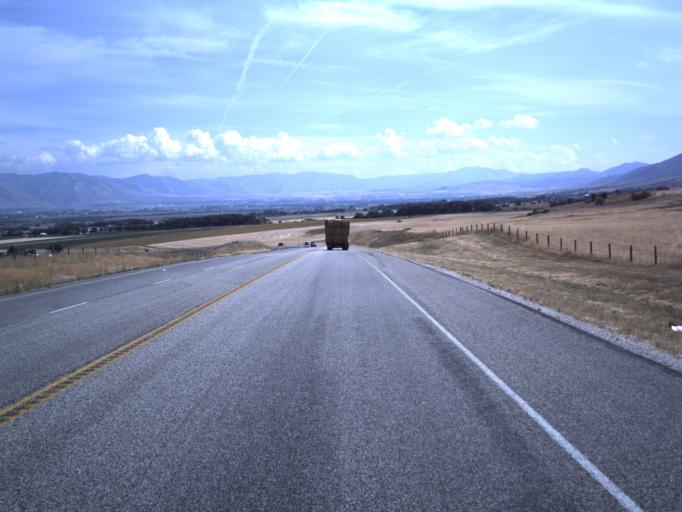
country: US
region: Utah
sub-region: Cache County
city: Mendon
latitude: 41.7610
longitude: -112.0073
